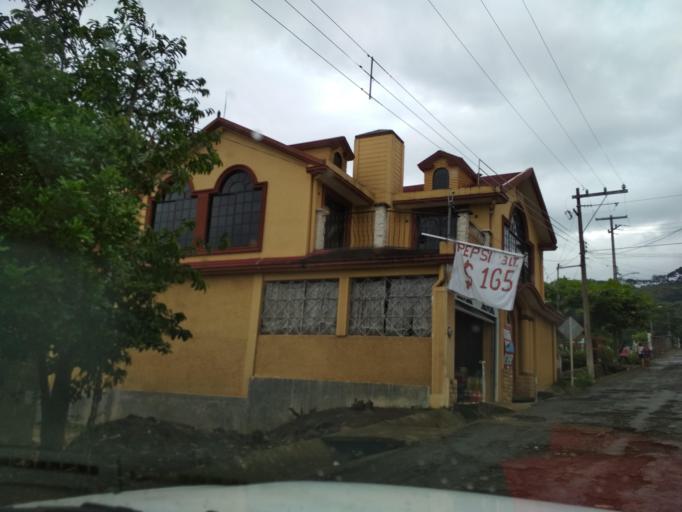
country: MX
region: Veracruz
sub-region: San Andres Tuxtla
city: San Isidro Xoteapan (San Isidro Texcaltitan)
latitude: 18.4628
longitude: -95.2344
